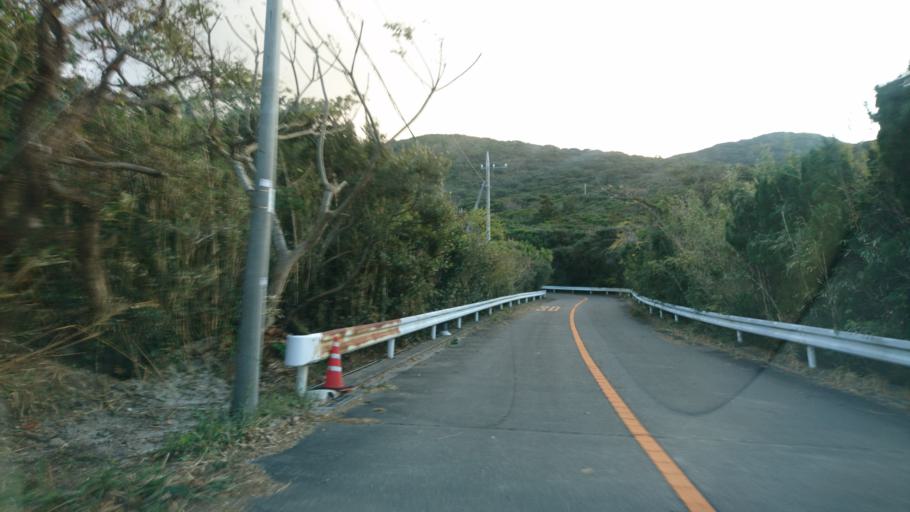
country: JP
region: Shizuoka
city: Shimoda
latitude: 34.3631
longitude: 139.2558
